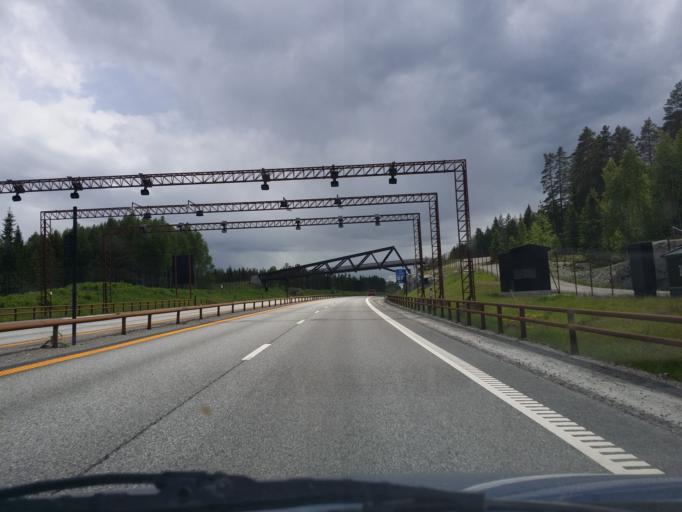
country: NO
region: Akershus
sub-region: Eidsvoll
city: Raholt
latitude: 60.3069
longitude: 11.1413
